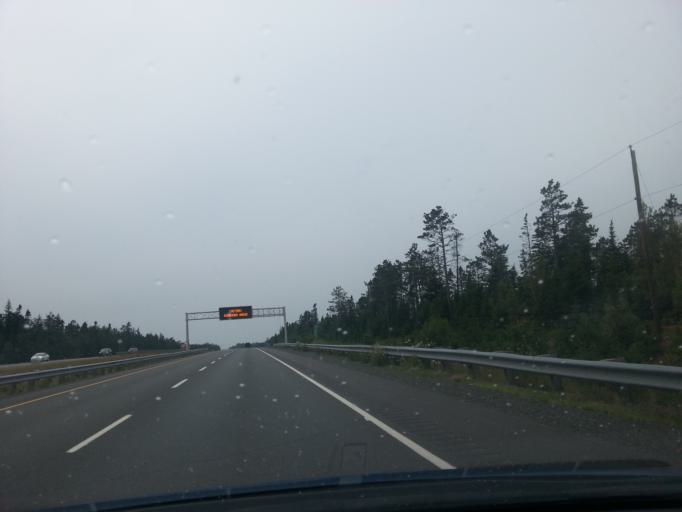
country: CA
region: Nova Scotia
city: Truro
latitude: 45.3984
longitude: -63.4494
